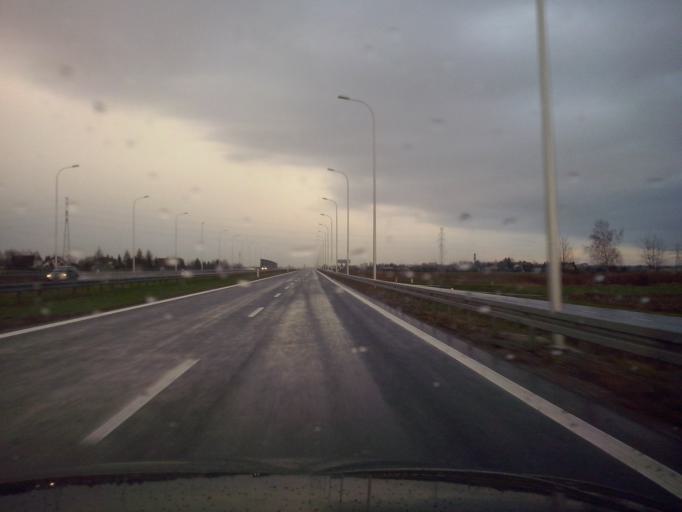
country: PL
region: Lublin Voivodeship
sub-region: Powiat lubelski
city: Jastkow
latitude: 51.2745
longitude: 22.4763
